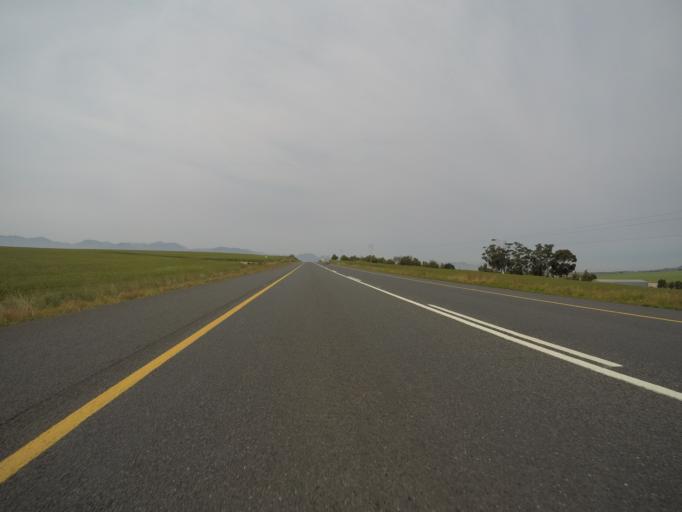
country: ZA
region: Western Cape
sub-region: Cape Winelands District Municipality
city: Noorder-Paarl
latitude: -33.5570
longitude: 18.8755
